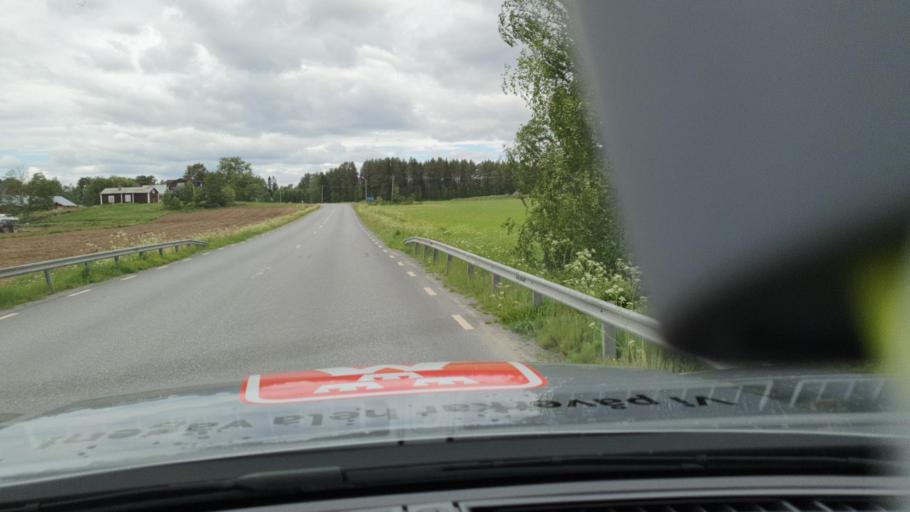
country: SE
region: Norrbotten
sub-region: Lulea Kommun
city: Sodra Sunderbyn
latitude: 65.8224
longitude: 21.9917
